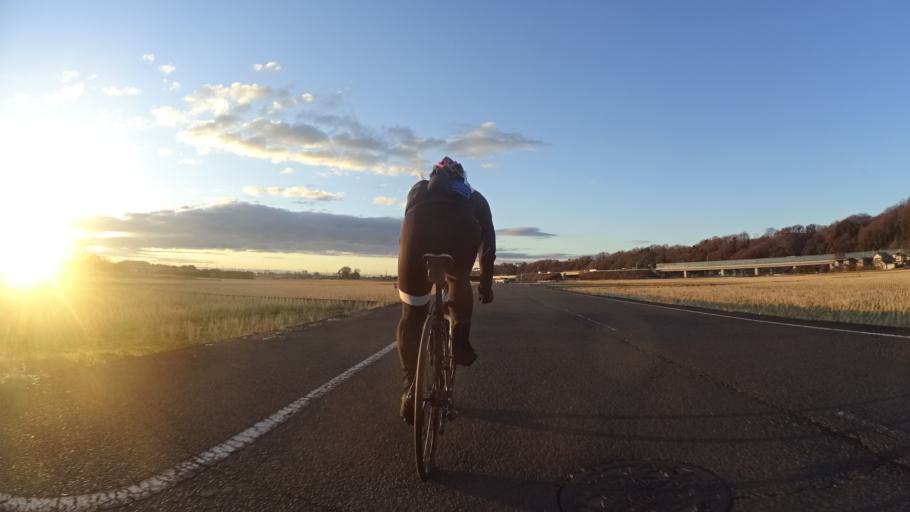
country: JP
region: Kanagawa
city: Zama
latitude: 35.5111
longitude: 139.3677
